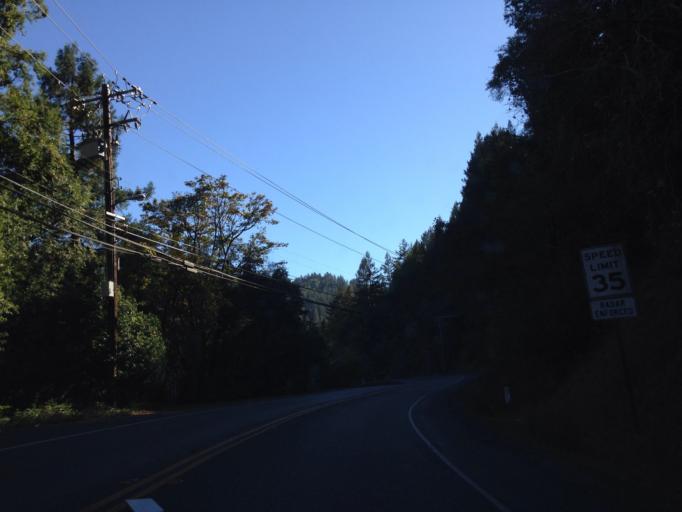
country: US
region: California
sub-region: Sonoma County
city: Guerneville
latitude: 38.5000
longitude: -123.0055
